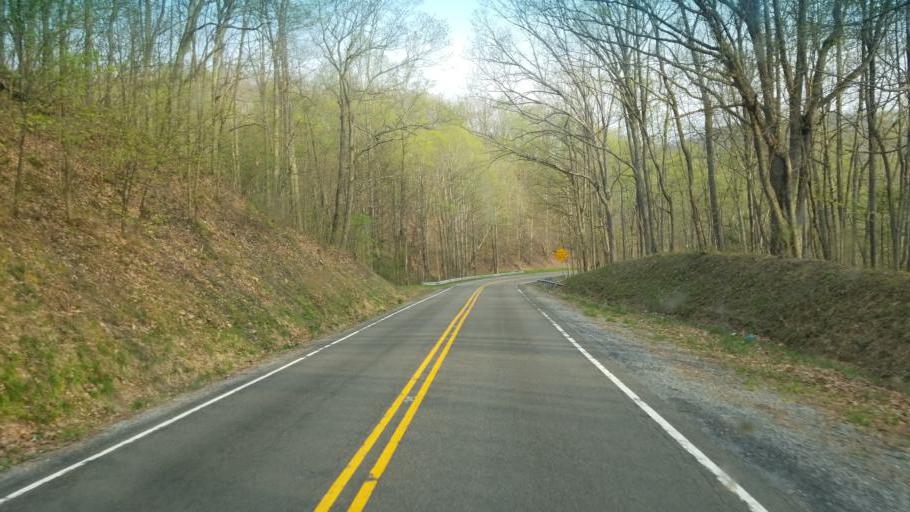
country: US
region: Virginia
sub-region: Smyth County
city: Atkins
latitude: 36.8160
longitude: -81.4270
